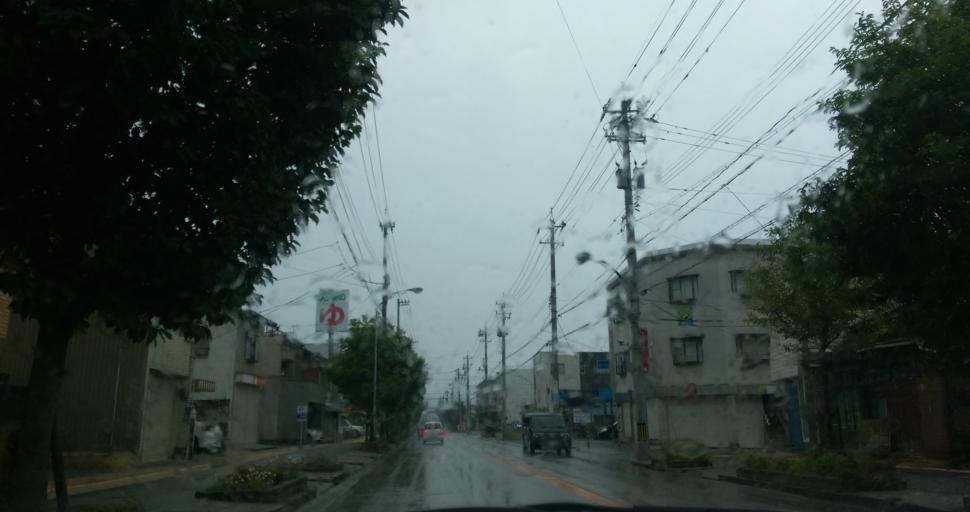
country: JP
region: Fukui
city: Fukui-shi
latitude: 36.0617
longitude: 136.2055
